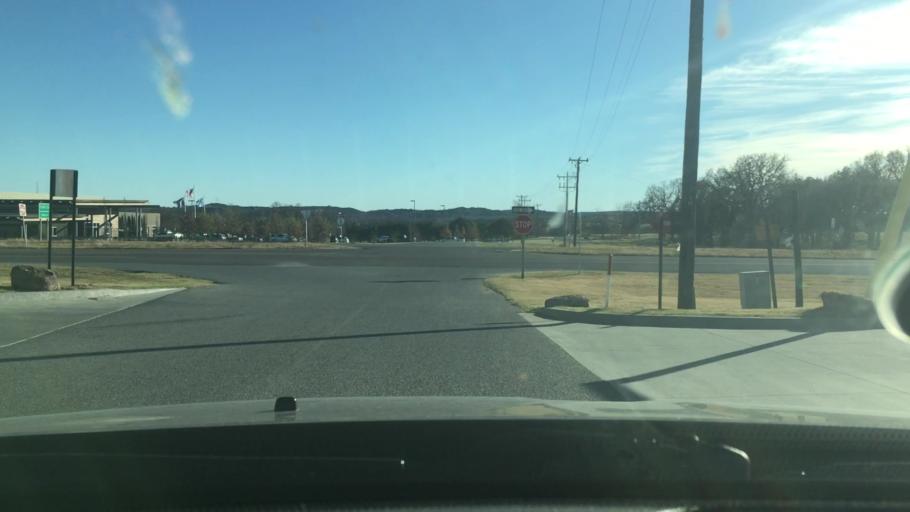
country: US
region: Oklahoma
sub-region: Murray County
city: Davis
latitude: 34.5072
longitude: -97.1774
